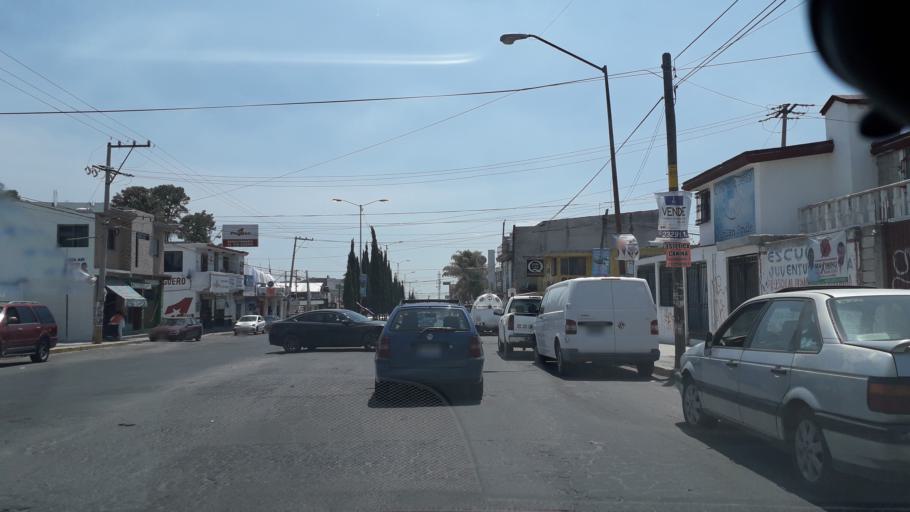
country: MX
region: Puebla
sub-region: Puebla
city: Primero de Mayo
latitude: 19.0723
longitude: -98.1150
